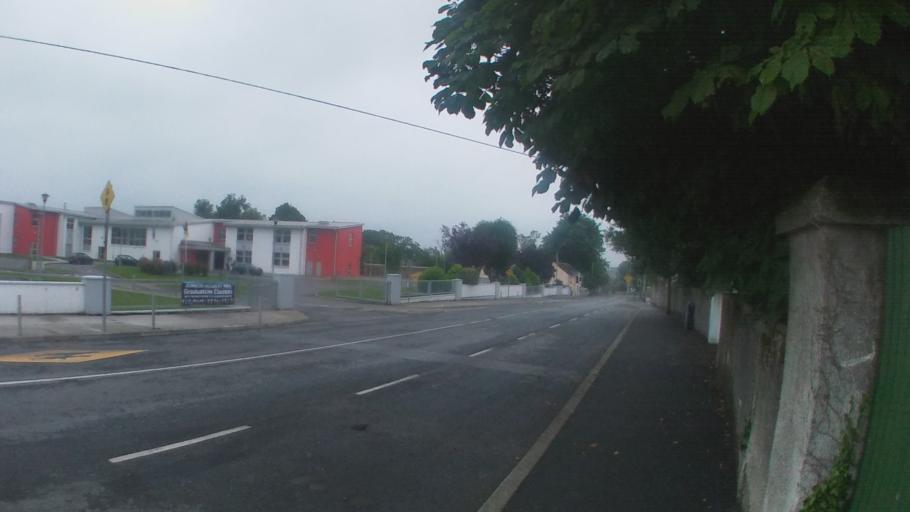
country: IE
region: Leinster
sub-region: Kilkenny
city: Callan
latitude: 52.5486
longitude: -7.3879
